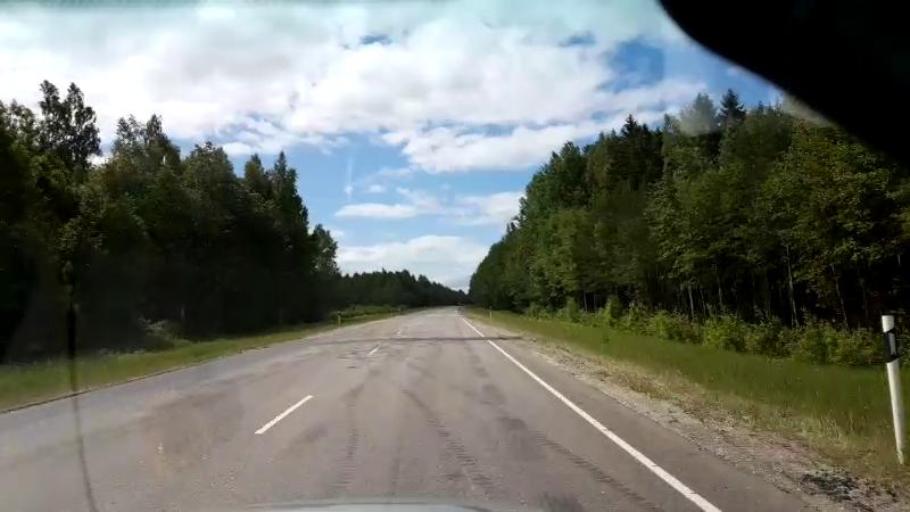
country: LV
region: Salacgrivas
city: Ainazi
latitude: 58.0229
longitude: 24.5003
